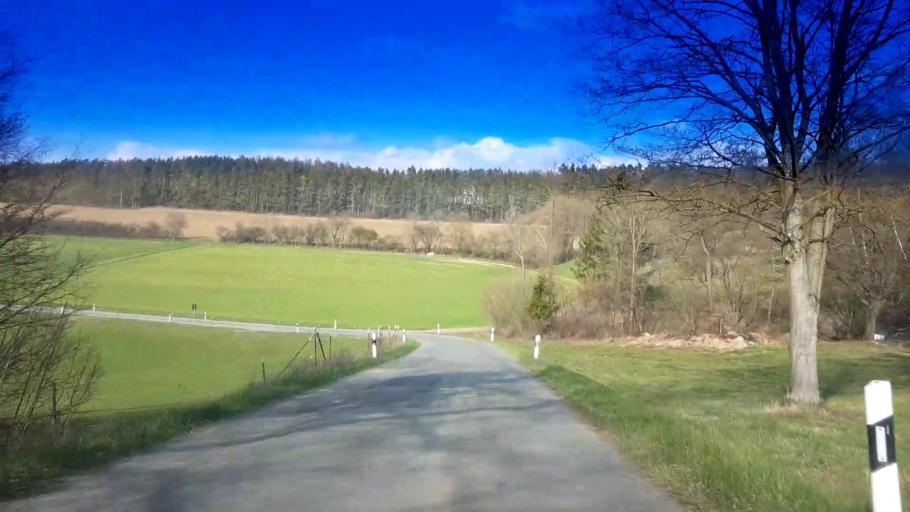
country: DE
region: Bavaria
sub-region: Upper Franconia
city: Harsdorf
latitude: 50.0319
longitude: 11.5882
